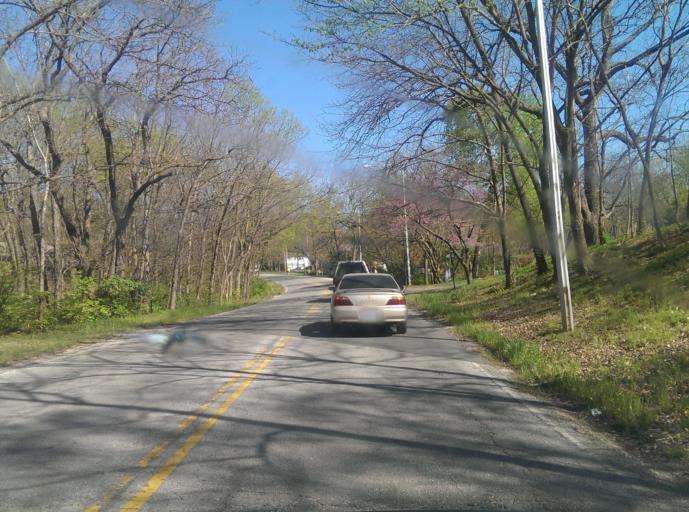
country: US
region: Kansas
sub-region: Johnson County
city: Leawood
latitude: 38.9274
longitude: -94.6015
